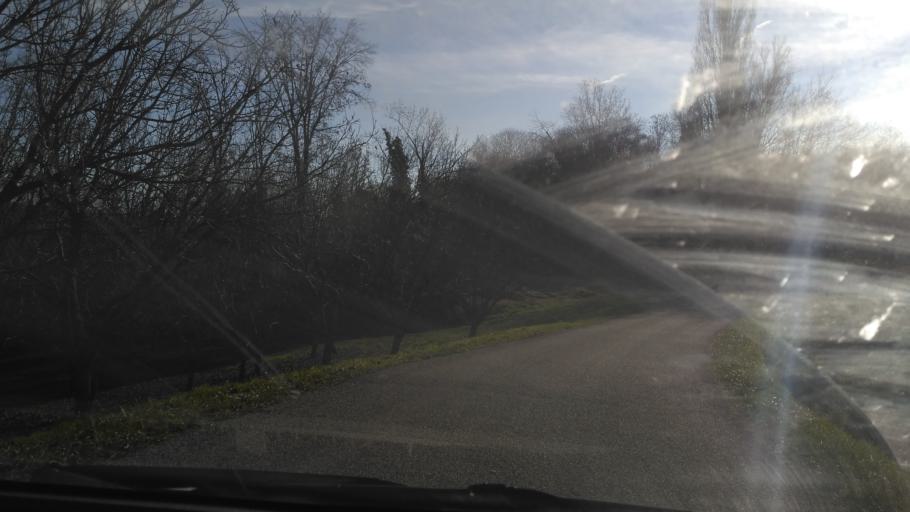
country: FR
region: Rhone-Alpes
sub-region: Departement de l'Isere
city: Saint-Antoine-l'Abbaye
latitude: 45.1485
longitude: 5.1425
